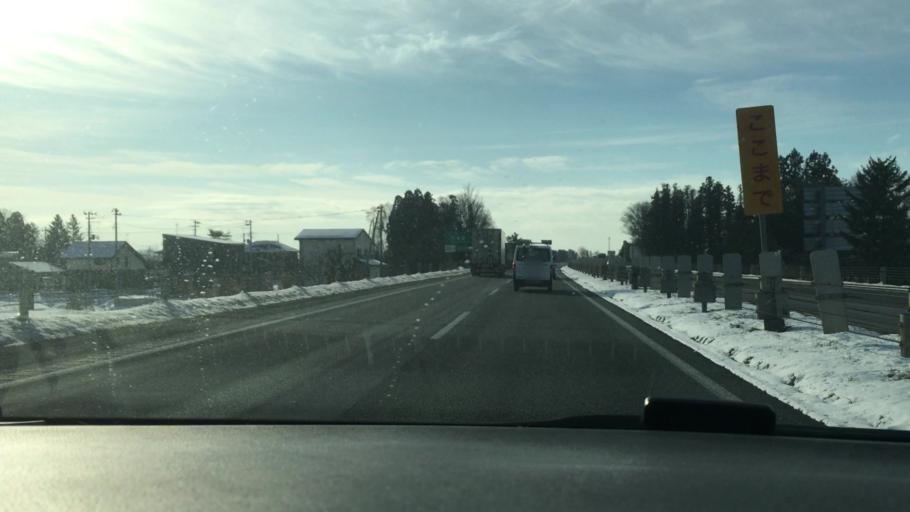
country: JP
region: Iwate
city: Hanamaki
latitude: 39.3992
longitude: 141.0926
